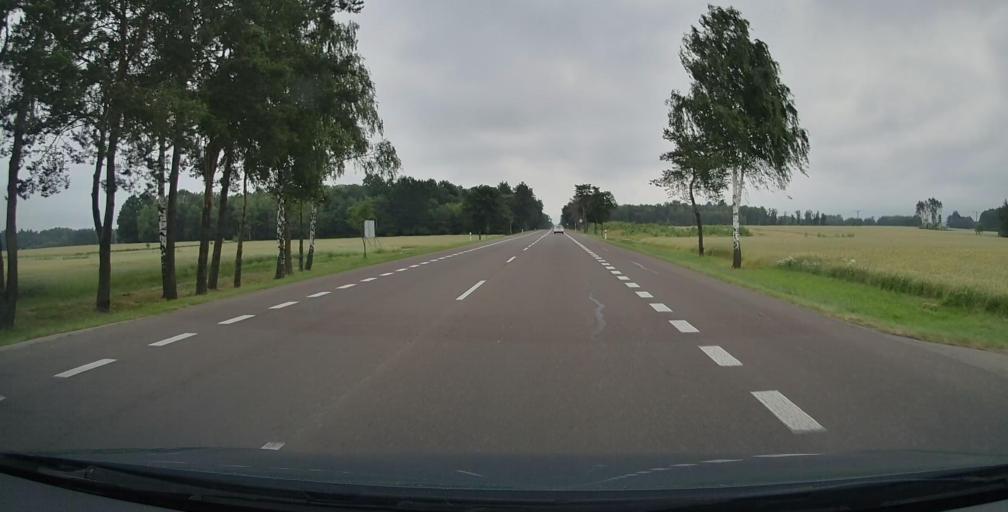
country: PL
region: Lublin Voivodeship
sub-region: Powiat bialski
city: Miedzyrzec Podlaski
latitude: 52.0092
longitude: 22.8324
